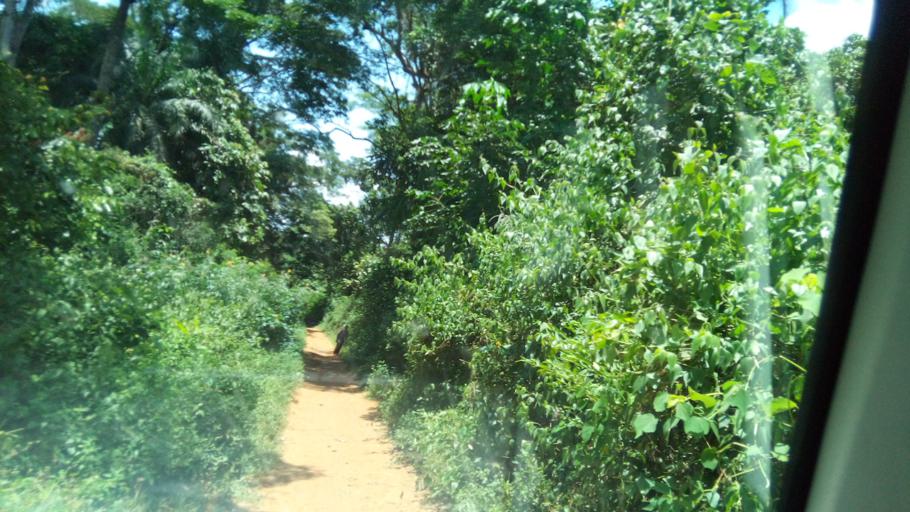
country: AO
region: Zaire
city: Mbanza Congo
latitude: -5.8041
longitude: 14.2447
